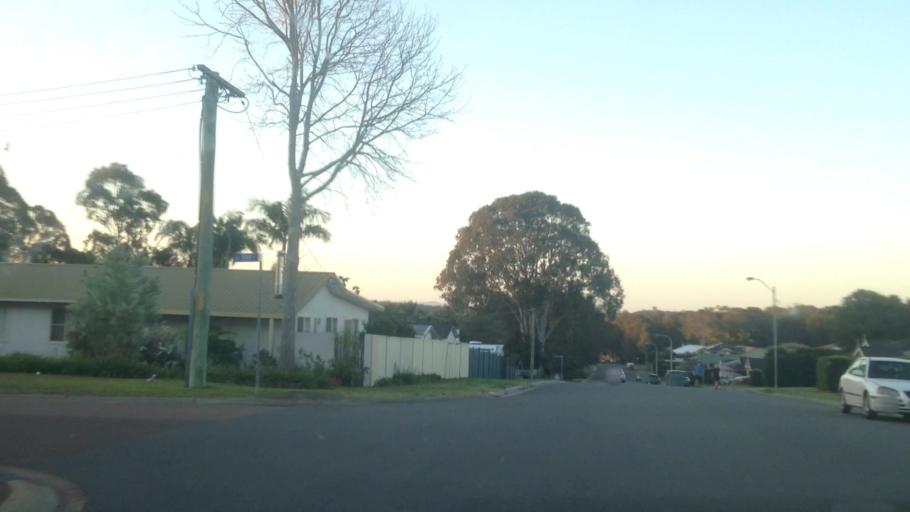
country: AU
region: New South Wales
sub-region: Wyong Shire
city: Kingfisher Shores
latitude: -33.1452
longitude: 151.5202
